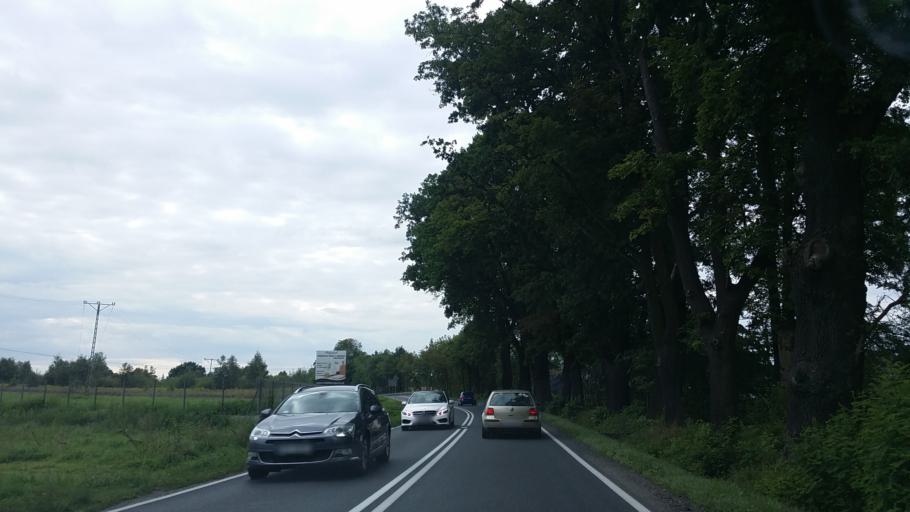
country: PL
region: Lesser Poland Voivodeship
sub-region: Powiat wadowicki
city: Sosnowice
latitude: 49.9593
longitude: 19.7010
